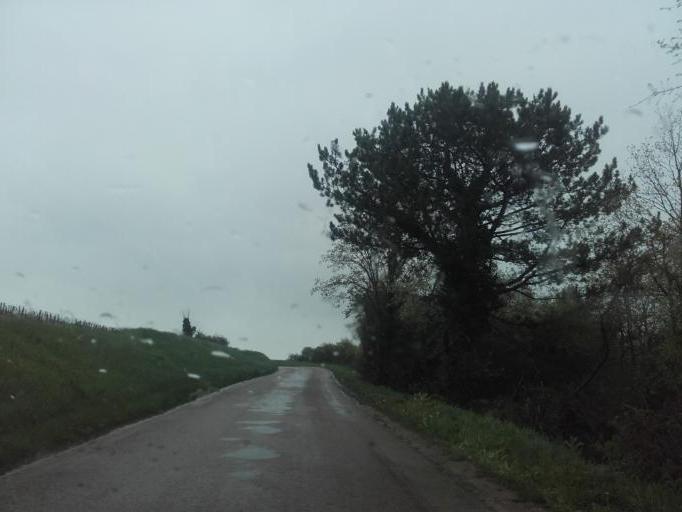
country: FR
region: Bourgogne
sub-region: Departement de l'Yonne
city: Chablis
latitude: 47.8010
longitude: 3.7904
